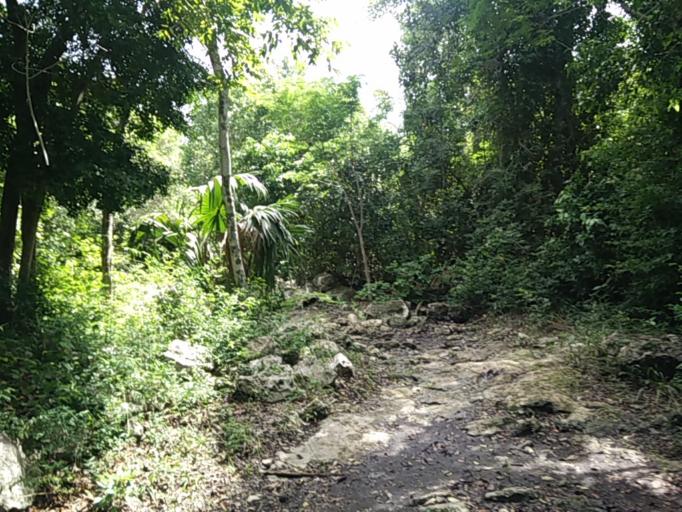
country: MX
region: Quintana Roo
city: San Miguel de Cozumel
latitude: 20.5035
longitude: -86.8455
